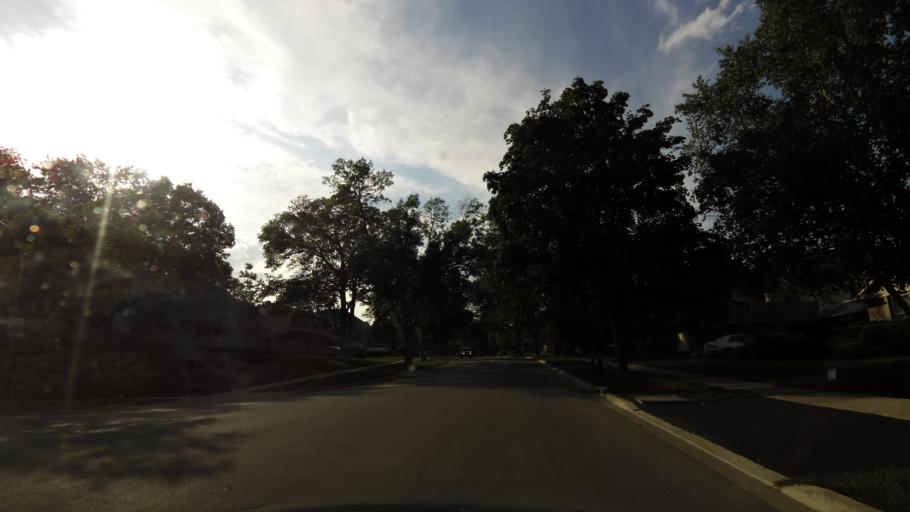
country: CA
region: Ontario
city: Burlington
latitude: 43.3450
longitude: -79.8460
